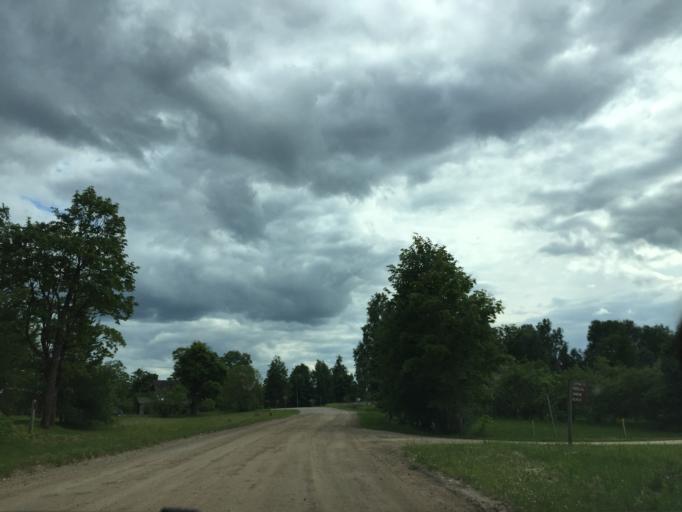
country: LV
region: Apes Novads
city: Ape
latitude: 57.5226
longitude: 26.3994
